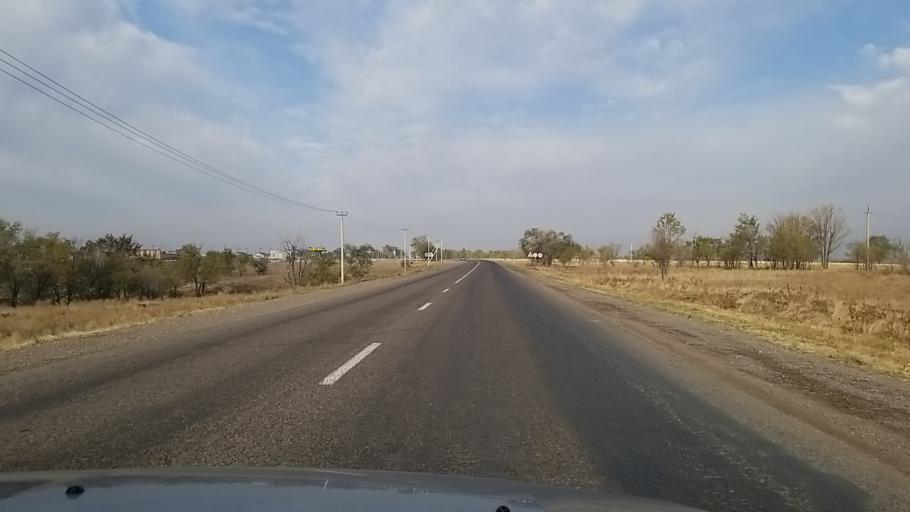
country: KZ
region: Almaty Oblysy
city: Burunday
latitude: 43.4760
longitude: 76.6882
